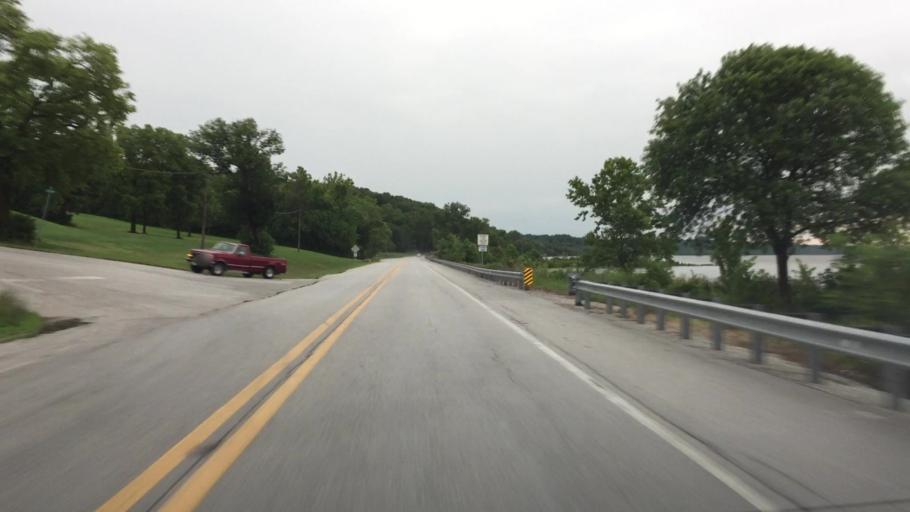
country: US
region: Illinois
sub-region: Hancock County
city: Nauvoo
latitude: 40.5123
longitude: -91.3590
